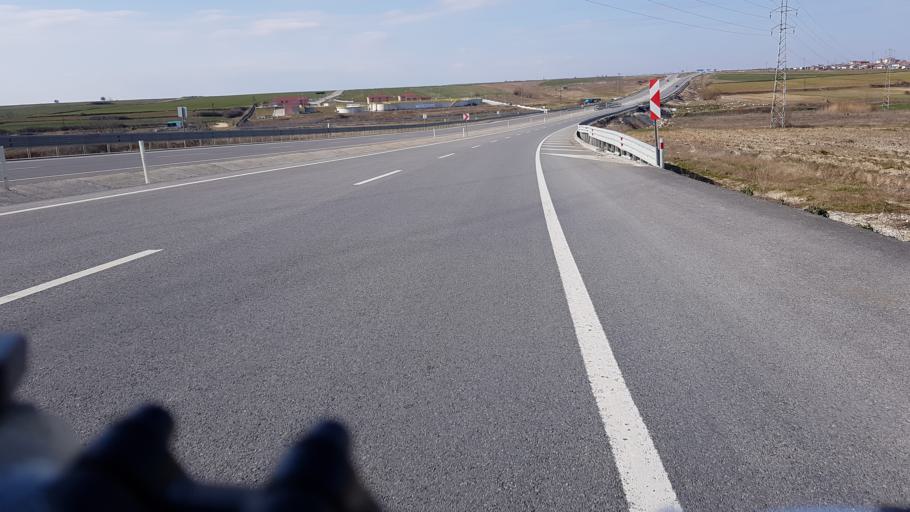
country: TR
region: Tekirdag
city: Saray
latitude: 41.4232
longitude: 27.9142
